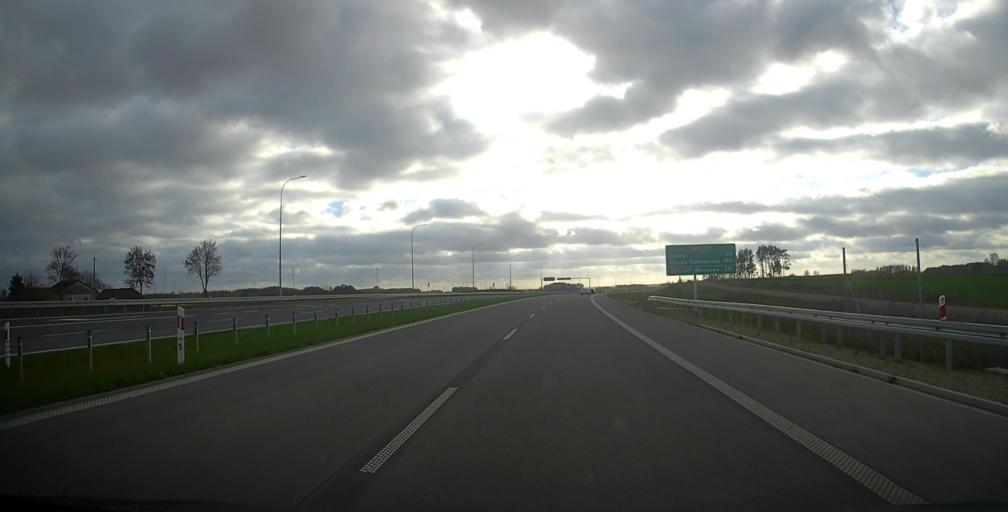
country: PL
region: Podlasie
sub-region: Powiat grajewski
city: Szczuczyn
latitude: 53.5868
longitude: 22.3264
